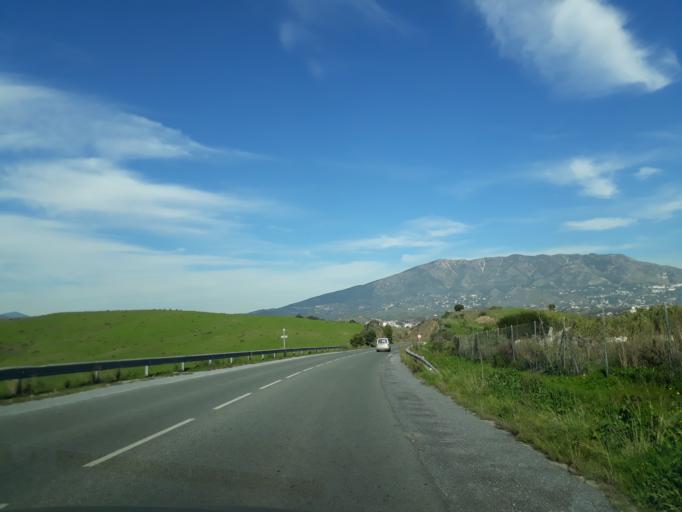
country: ES
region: Andalusia
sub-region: Provincia de Malaga
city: Fuengirola
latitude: 36.5332
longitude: -4.6860
